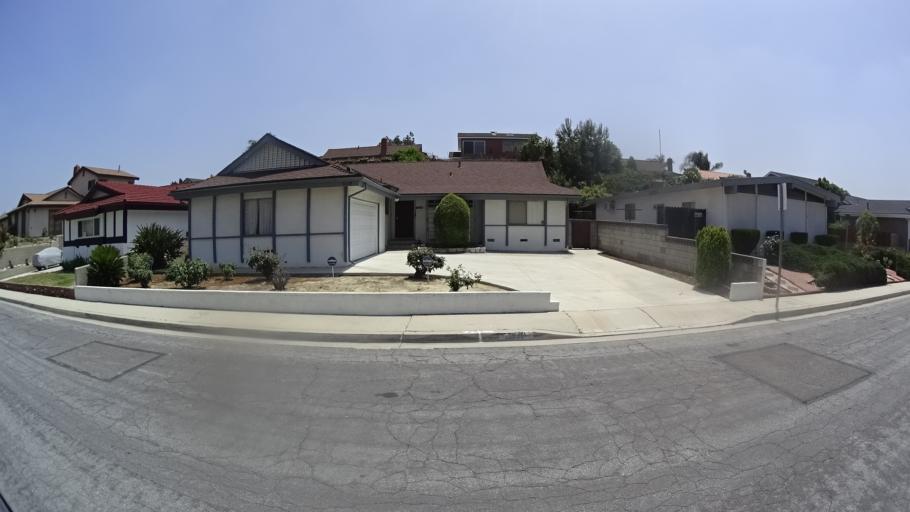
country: US
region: California
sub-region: Los Angeles County
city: Monterey Park
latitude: 34.0597
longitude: -118.1497
